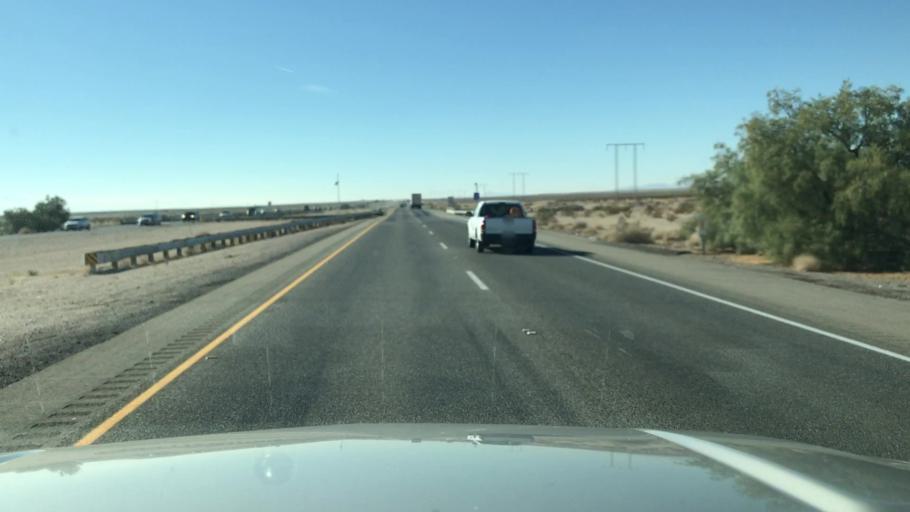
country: US
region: California
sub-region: San Bernardino County
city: Fort Irwin
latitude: 35.0253
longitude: -116.4920
